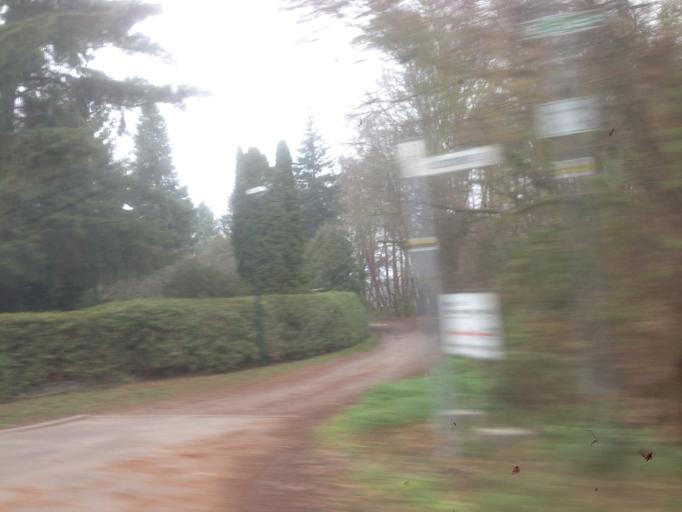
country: DE
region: Berlin
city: Blankenfelde
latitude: 52.6896
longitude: 13.3776
